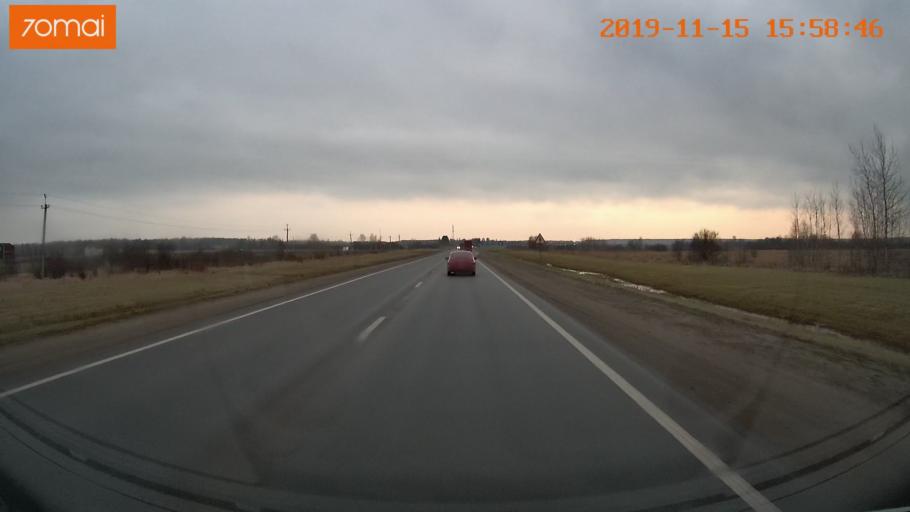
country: RU
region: Jaroslavl
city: Yaroslavl
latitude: 57.8154
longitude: 39.9524
